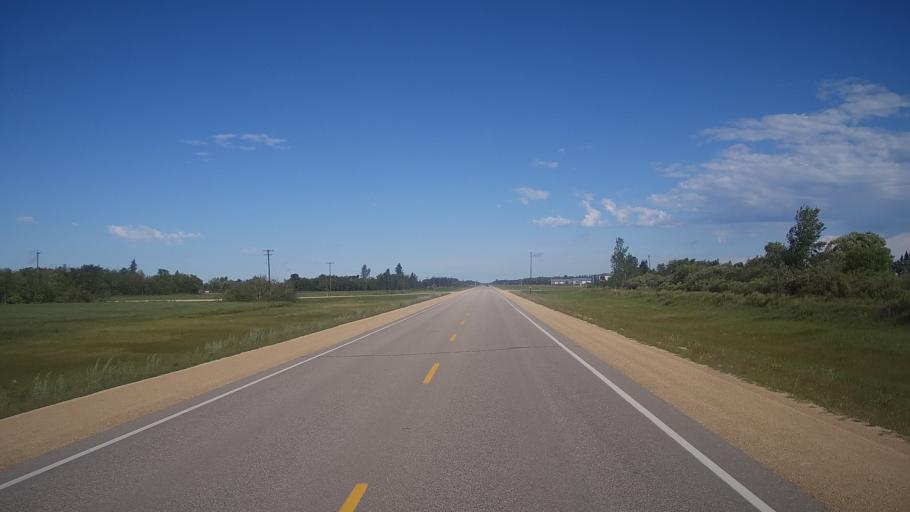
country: CA
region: Manitoba
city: Stonewall
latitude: 50.1934
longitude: -97.6411
